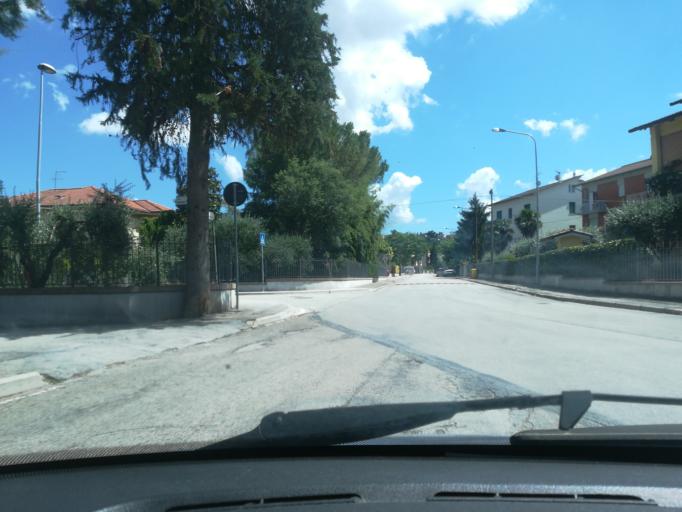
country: IT
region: The Marches
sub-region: Provincia di Macerata
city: Zona Industriale
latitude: 43.2634
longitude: 13.4945
